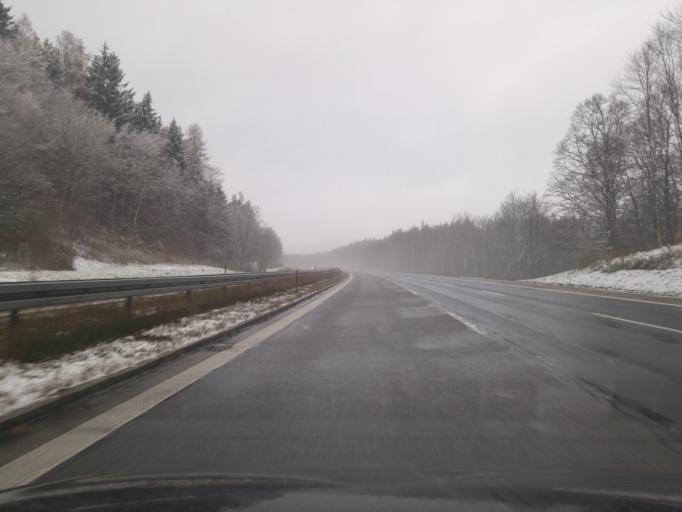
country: DE
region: Bavaria
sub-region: Regierungsbezirk Unterfranken
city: Elfershausen
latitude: 50.1713
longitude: 9.9628
